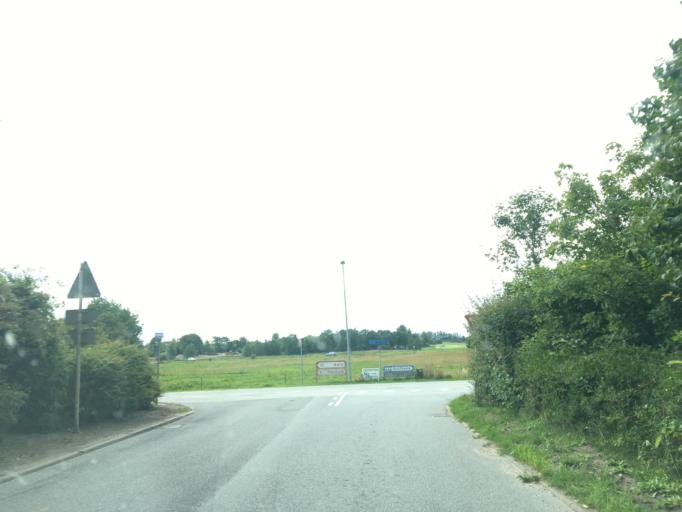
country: DK
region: North Denmark
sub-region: Vesthimmerland Kommune
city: Farso
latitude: 56.8794
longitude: 9.4041
